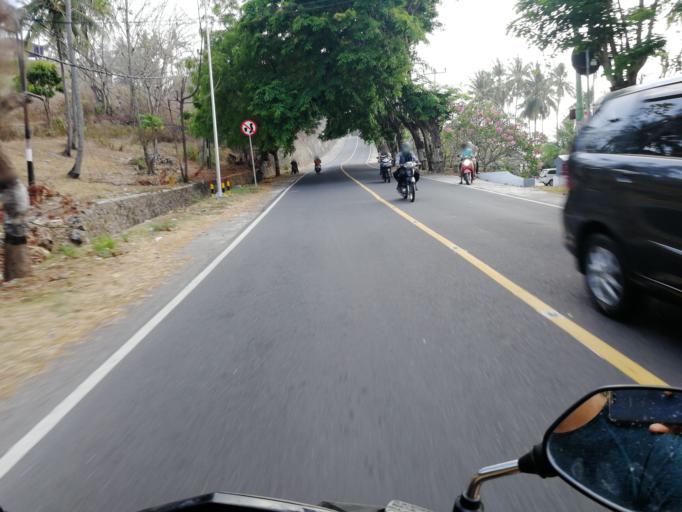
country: ID
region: West Nusa Tenggara
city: Mambalan
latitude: -8.4926
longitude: 116.0399
